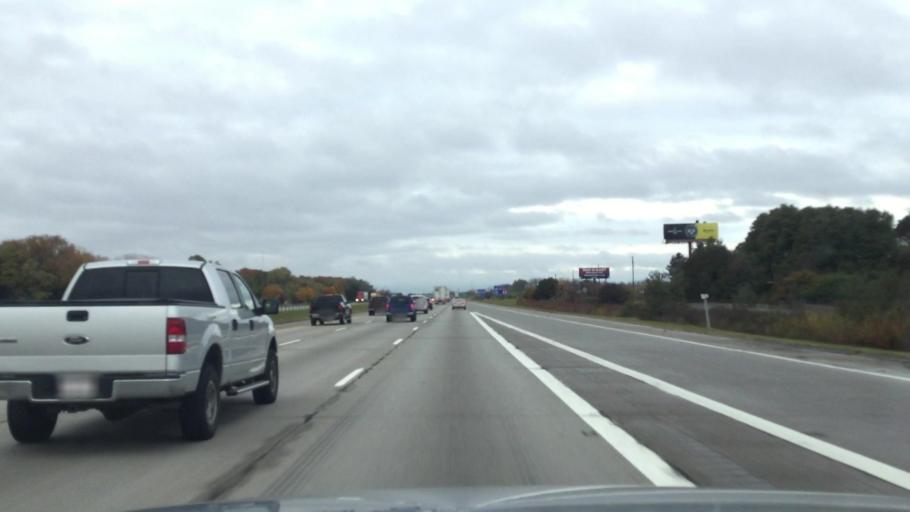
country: US
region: Michigan
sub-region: Wayne County
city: Belleville
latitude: 42.2186
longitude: -83.5245
